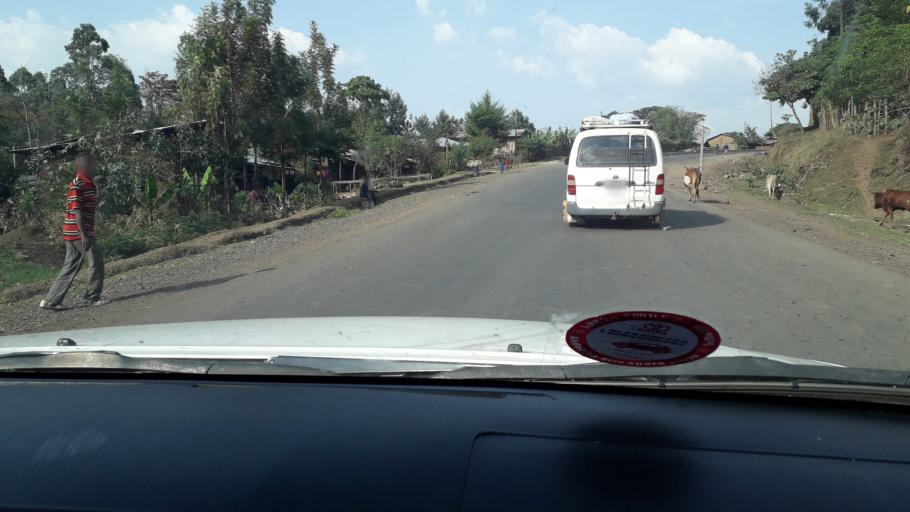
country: ET
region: Southern Nations, Nationalities, and People's Region
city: Mizan Teferi
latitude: 6.9326
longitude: 35.4919
